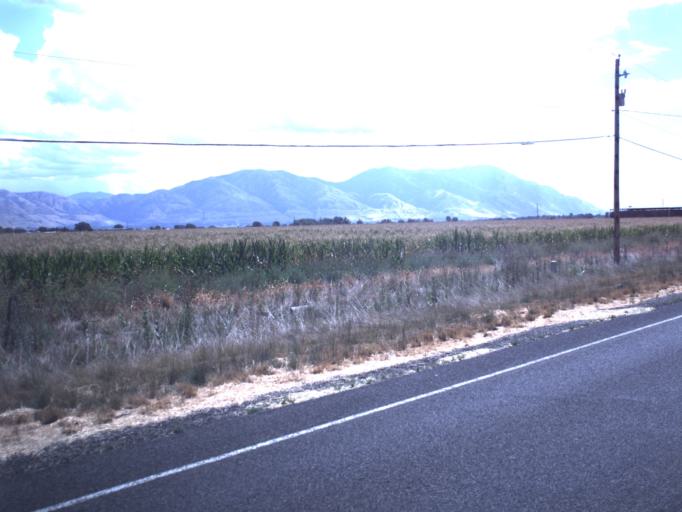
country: US
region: Utah
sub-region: Box Elder County
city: Honeyville
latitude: 41.5871
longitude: -112.1298
